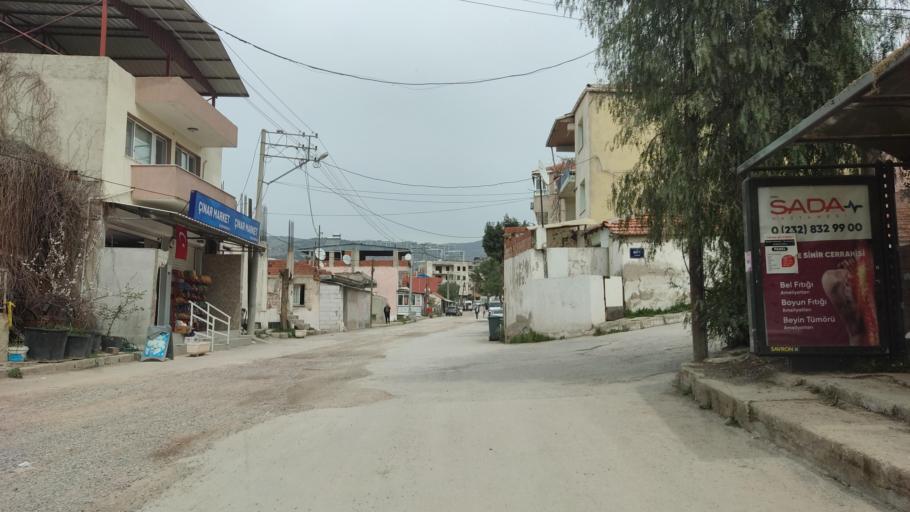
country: TR
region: Izmir
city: Karsiyaka
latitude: 38.4949
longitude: 27.0693
